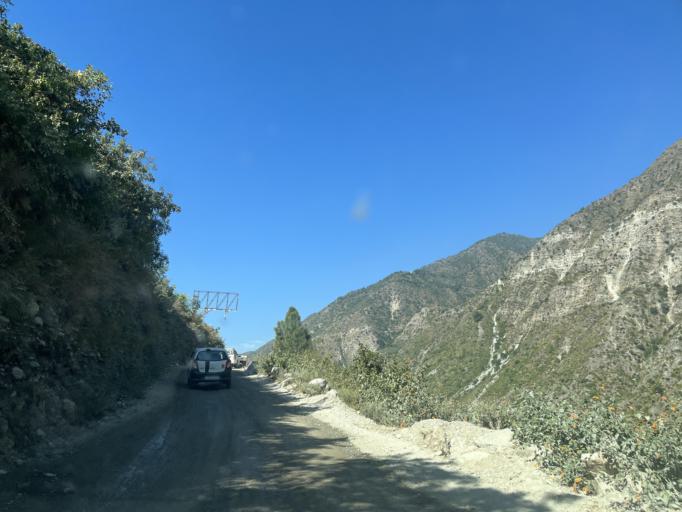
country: IN
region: Uttarakhand
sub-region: Almora
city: Ranikhet
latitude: 29.5515
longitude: 79.4014
